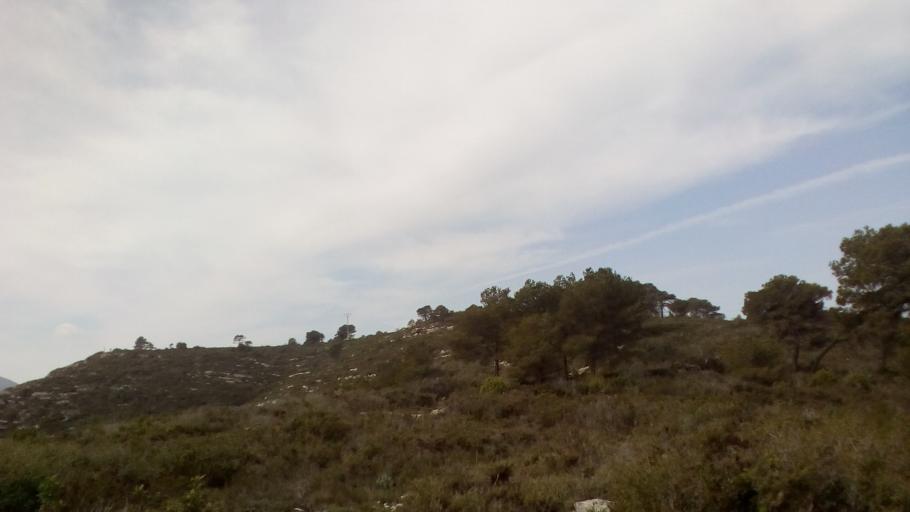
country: ES
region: Valencia
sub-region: Provincia de Valencia
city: Xeraco,Jaraco
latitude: 39.0389
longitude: -0.2454
